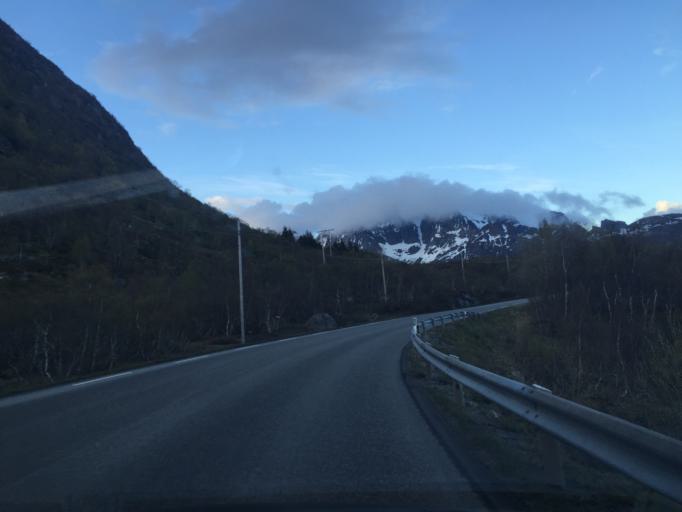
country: NO
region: Nordland
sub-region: Vagan
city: Svolvaer
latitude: 68.2839
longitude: 14.6611
